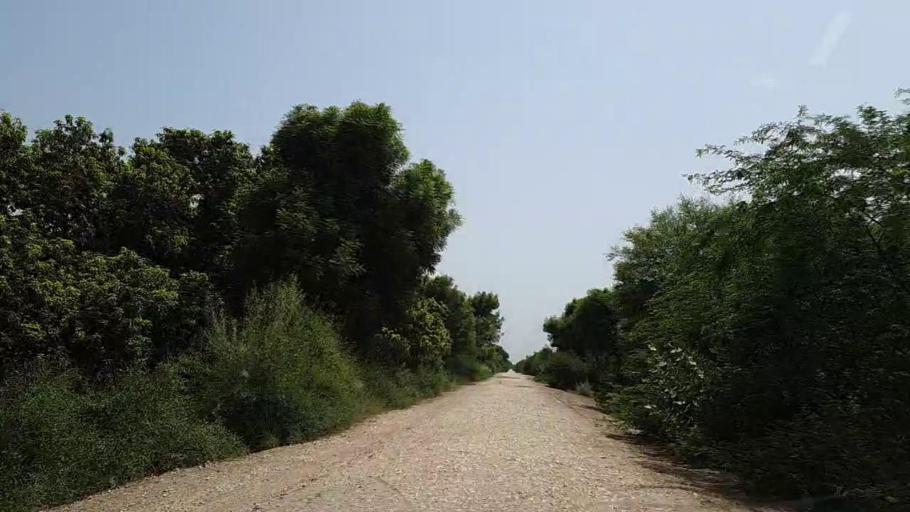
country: PK
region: Sindh
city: Kandiaro
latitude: 27.0368
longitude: 68.1268
